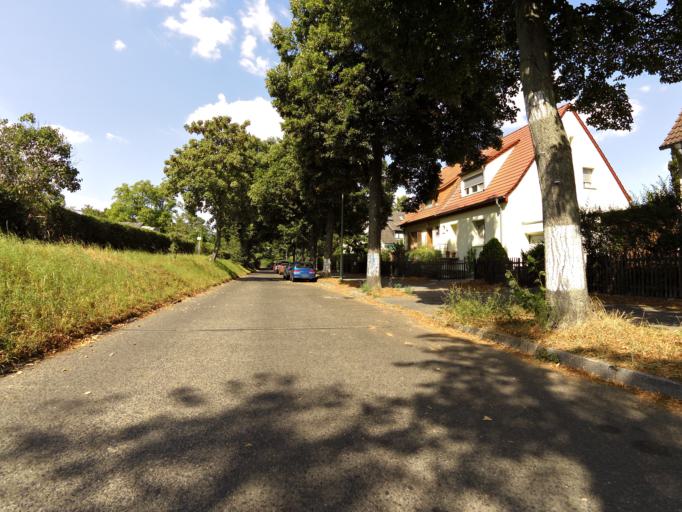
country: DE
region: Berlin
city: Lankwitz
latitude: 52.4422
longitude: 13.3496
